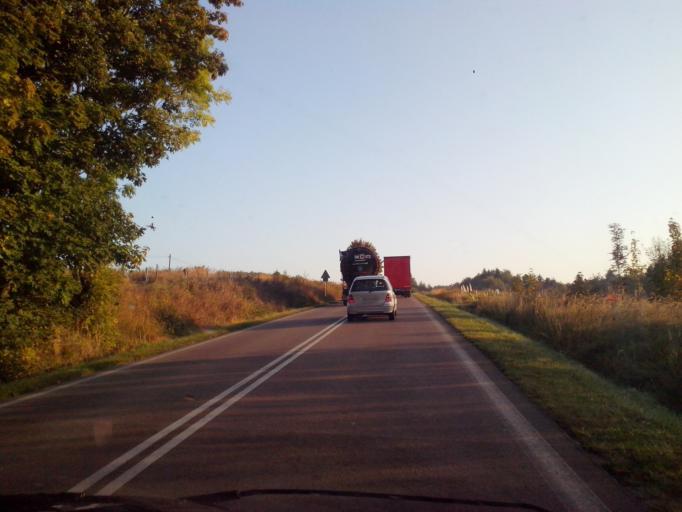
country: PL
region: Subcarpathian Voivodeship
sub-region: Powiat brzozowski
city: Golcowa
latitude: 49.8164
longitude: 22.0508
